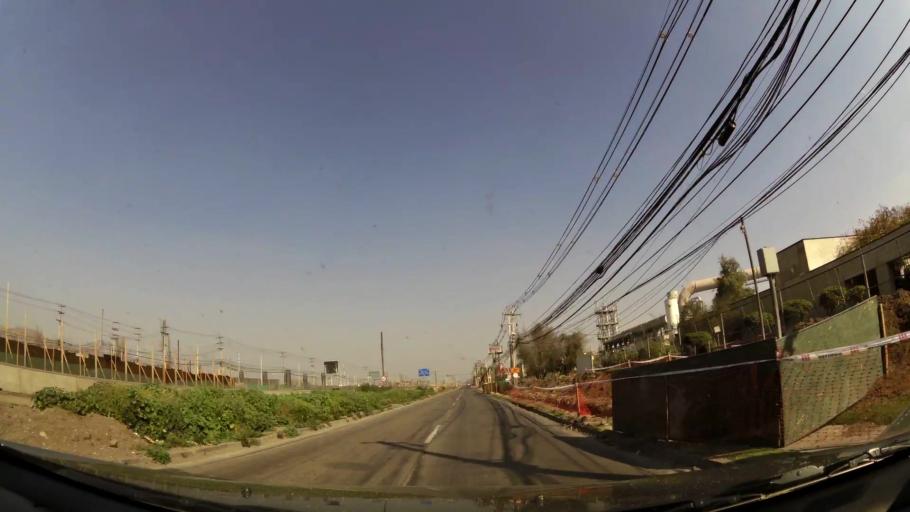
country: CL
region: Santiago Metropolitan
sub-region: Provincia de Chacabuco
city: Chicureo Abajo
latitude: -33.3450
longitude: -70.7102
